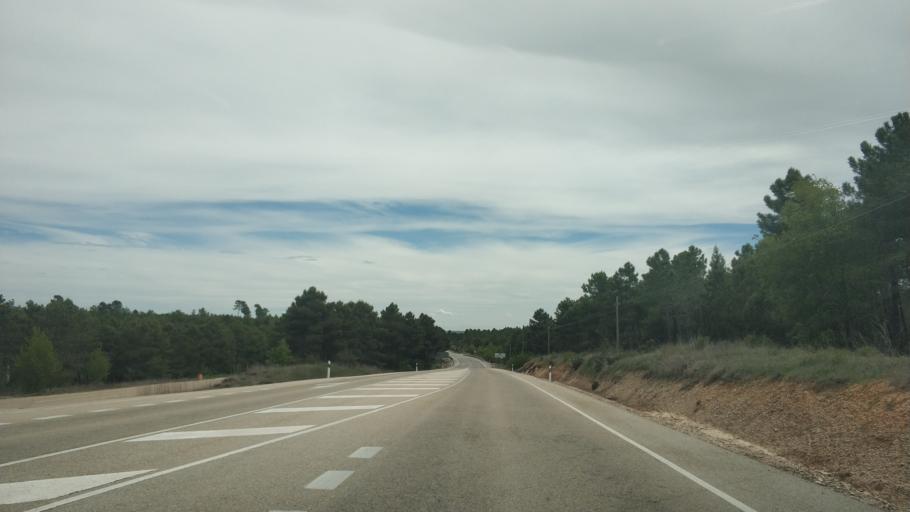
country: ES
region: Castille and Leon
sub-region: Provincia de Soria
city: Valdenebro
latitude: 41.5402
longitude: -2.9544
